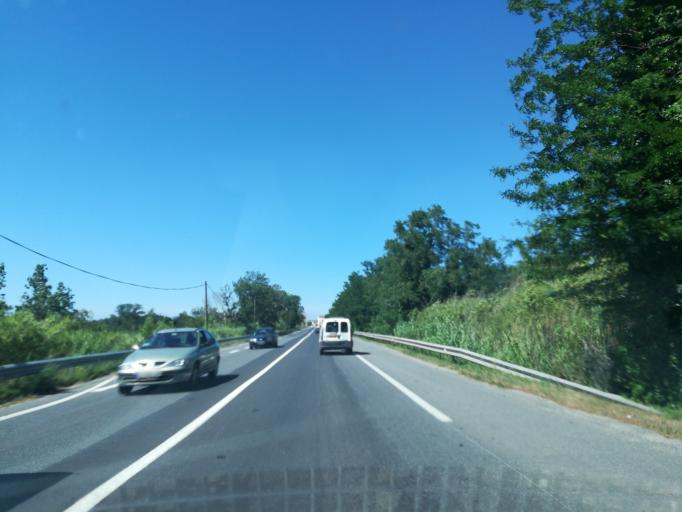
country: FR
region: Languedoc-Roussillon
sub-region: Departement des Pyrenees-Orientales
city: Villemolaque
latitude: 42.6047
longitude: 2.8586
